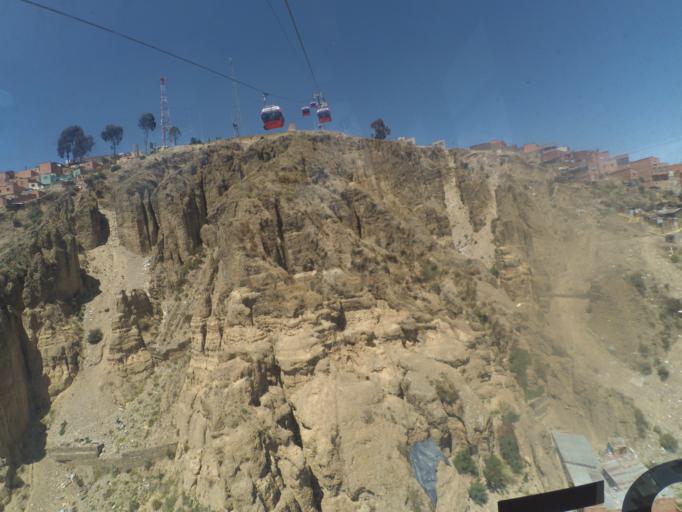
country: BO
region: La Paz
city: La Paz
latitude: -16.4976
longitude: -68.1610
